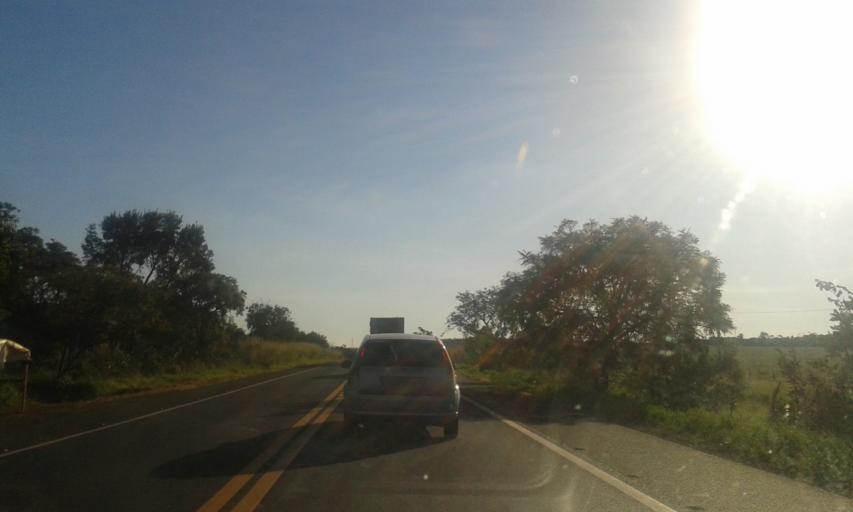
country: BR
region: Minas Gerais
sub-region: Monte Alegre De Minas
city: Monte Alegre de Minas
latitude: -18.8804
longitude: -49.1768
